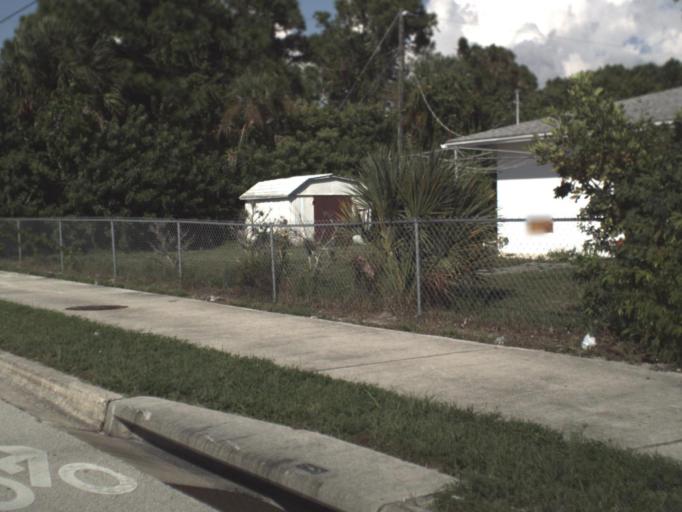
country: US
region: Florida
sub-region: Sarasota County
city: Englewood
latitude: 26.9677
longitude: -82.3529
